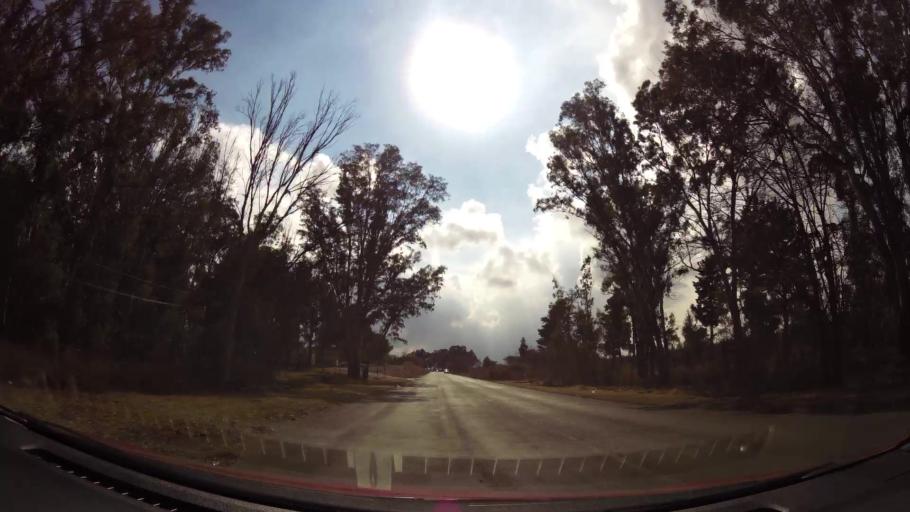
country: ZA
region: Gauteng
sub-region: Sedibeng District Municipality
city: Vanderbijlpark
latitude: -26.7445
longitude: 27.8240
